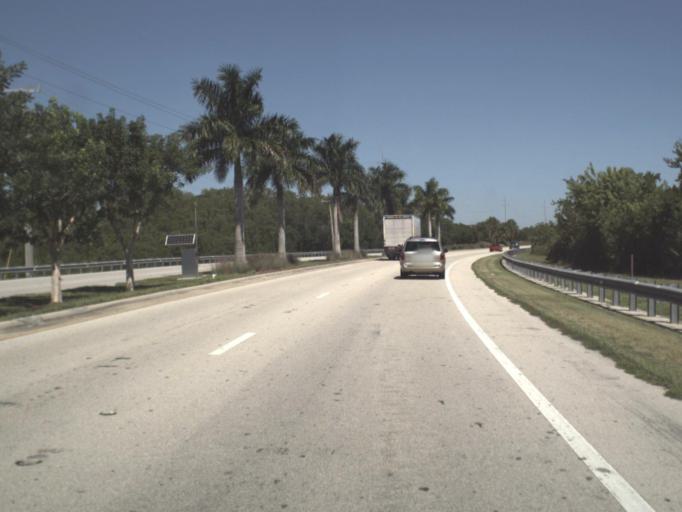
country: US
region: Florida
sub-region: Collier County
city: Marco
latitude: 25.9692
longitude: -81.7078
